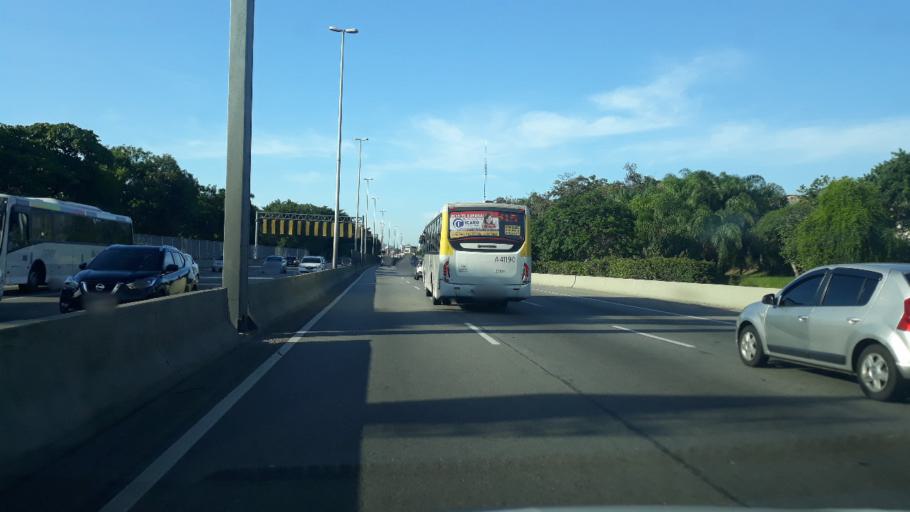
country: BR
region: Rio de Janeiro
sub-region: Sao Joao De Meriti
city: Sao Joao de Meriti
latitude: -22.9456
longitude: -43.3542
